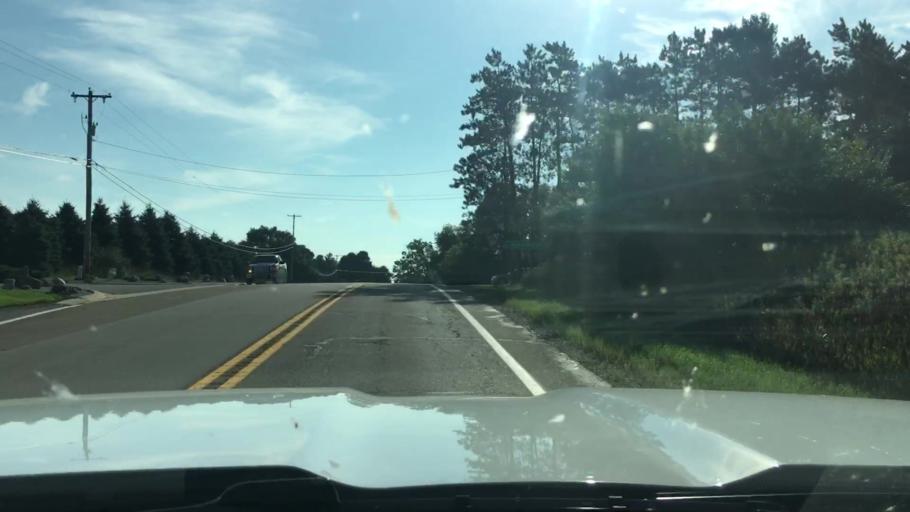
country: US
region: Michigan
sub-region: Kent County
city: Sparta
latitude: 43.2195
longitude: -85.6545
